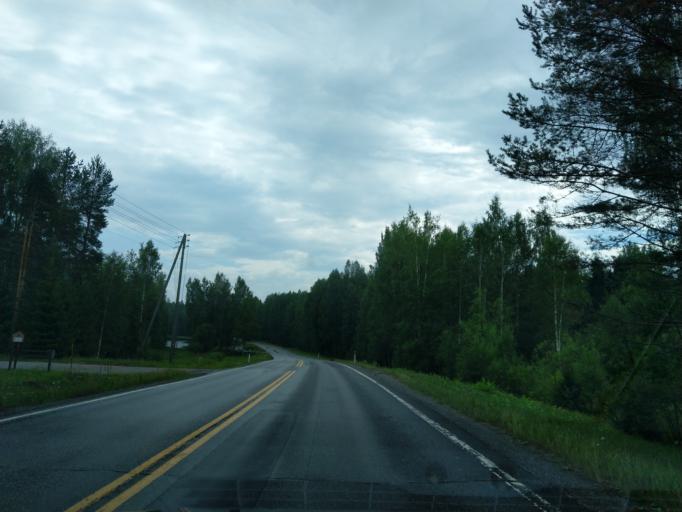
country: FI
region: Southern Savonia
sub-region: Savonlinna
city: Punkaharju
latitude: 61.6673
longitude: 29.4120
